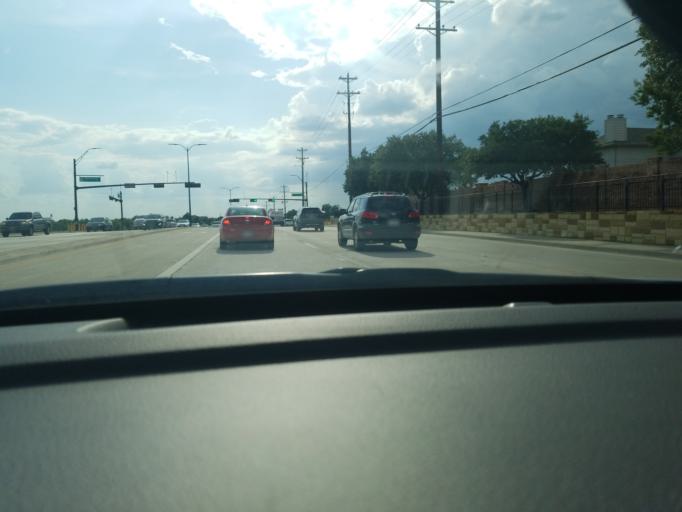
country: US
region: Texas
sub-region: Denton County
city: Little Elm
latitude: 33.1688
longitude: -96.9131
